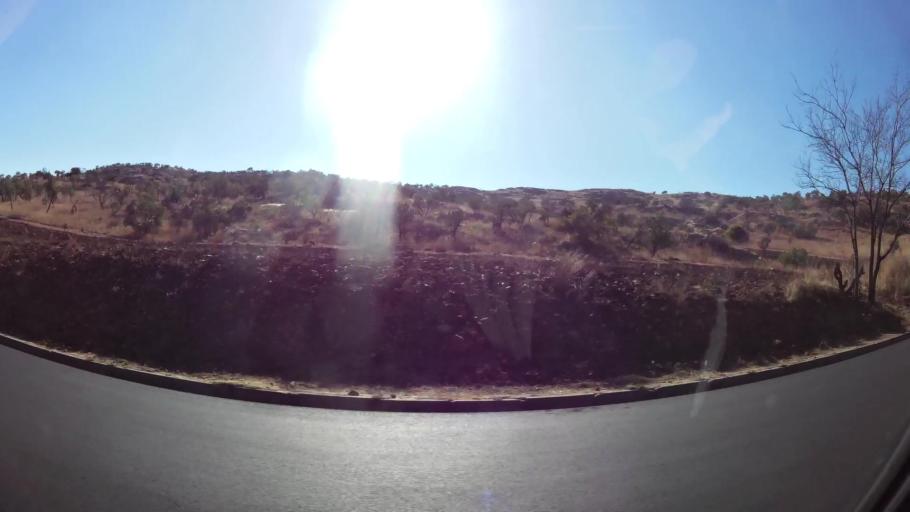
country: ZA
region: Gauteng
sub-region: City of Johannesburg Metropolitan Municipality
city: Roodepoort
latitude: -26.1274
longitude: 27.8828
